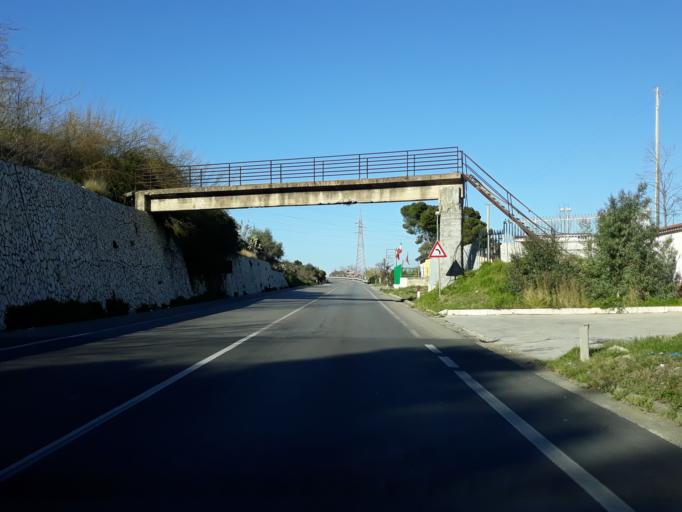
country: IT
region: Sicily
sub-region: Palermo
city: Misilmeri
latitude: 38.0371
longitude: 13.4599
